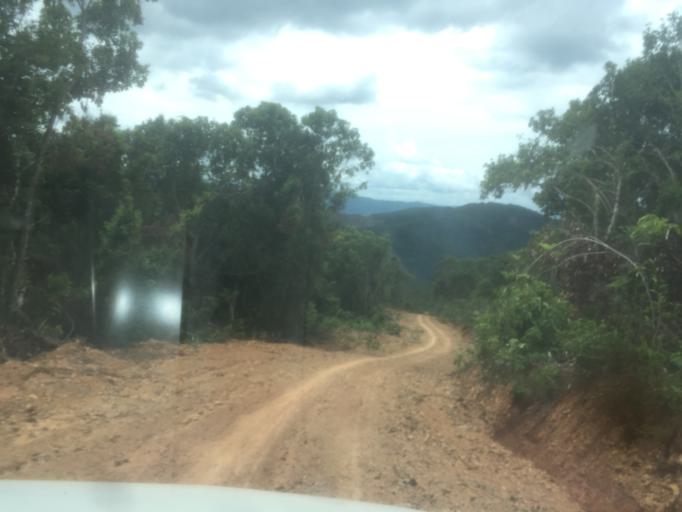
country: LA
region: Phongsali
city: Khoa
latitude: 20.9242
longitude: 102.5528
